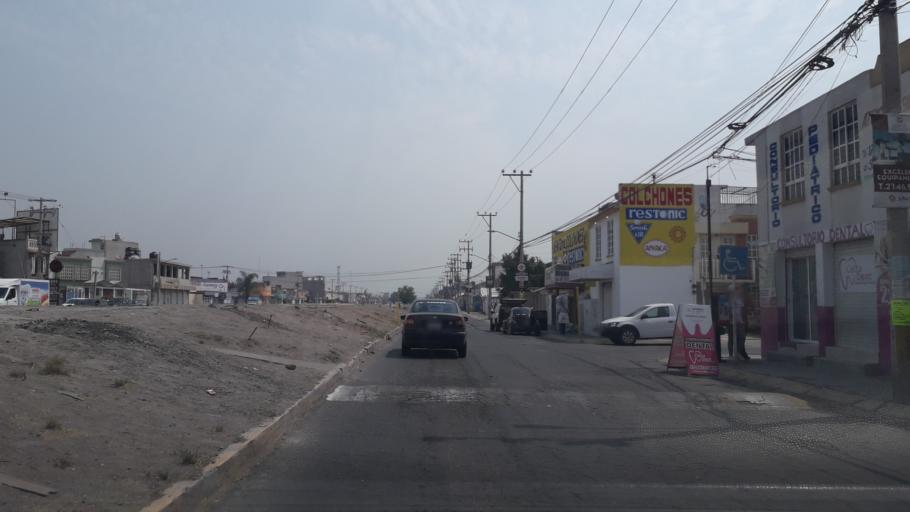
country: MX
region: Mexico
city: Santo Tomas Chiconautla
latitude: 19.6271
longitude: -99.0333
